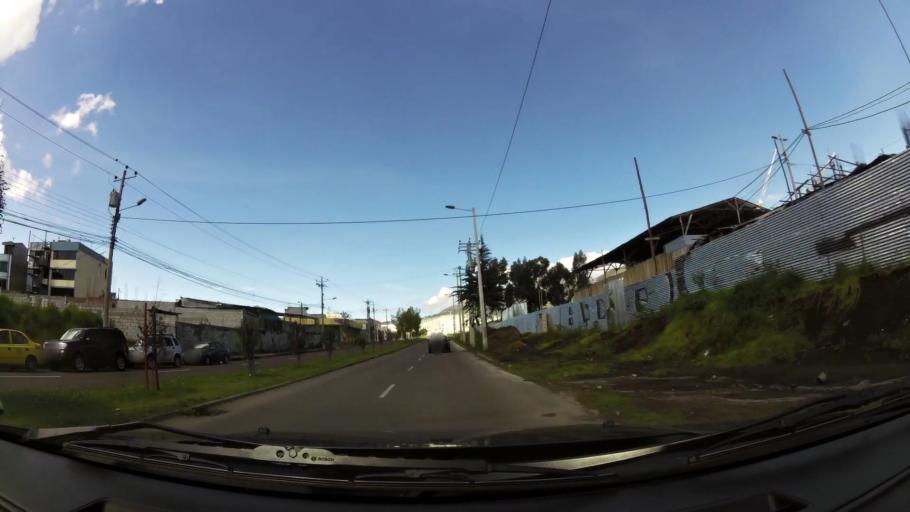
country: EC
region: Pichincha
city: Quito
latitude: -0.2934
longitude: -78.5448
